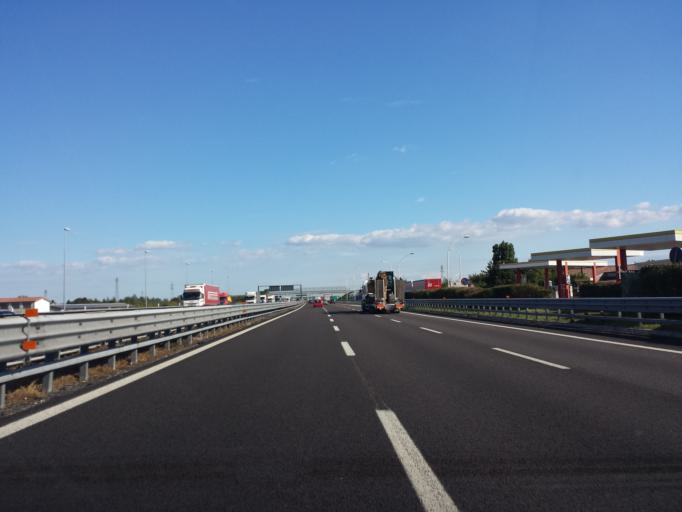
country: IT
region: Veneto
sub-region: Provincia di Vicenza
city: Torri di Quartesolo
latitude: 45.5048
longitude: 11.6246
